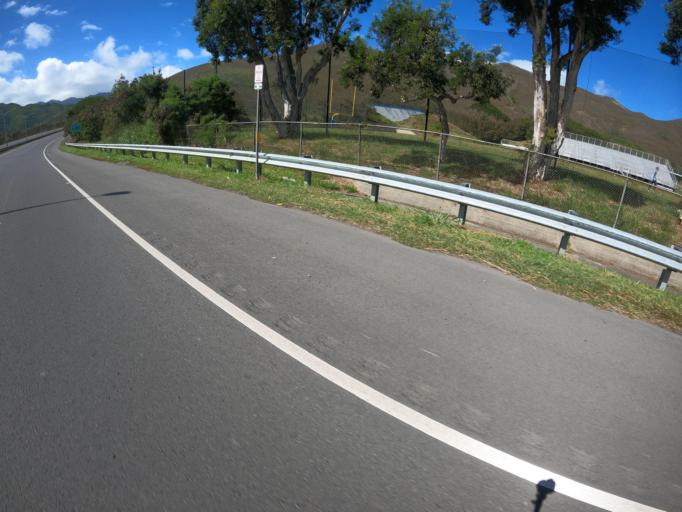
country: US
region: Hawaii
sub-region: Honolulu County
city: Kailua
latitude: 21.4067
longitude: -157.7594
